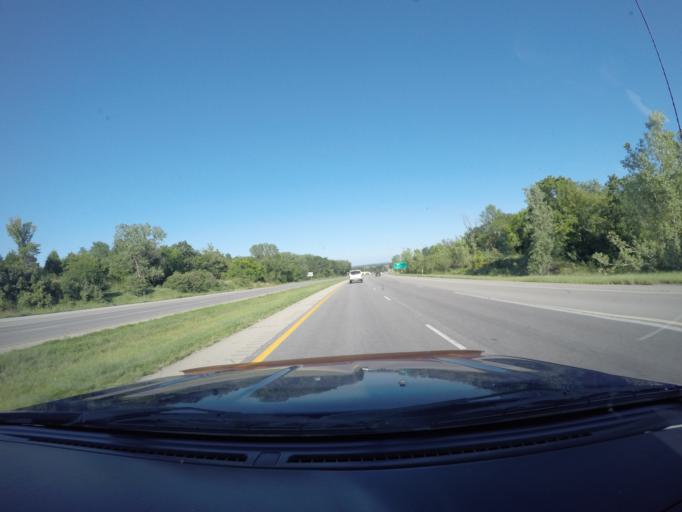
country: US
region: Kansas
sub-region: Shawnee County
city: Topeka
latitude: 39.0931
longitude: -95.6031
